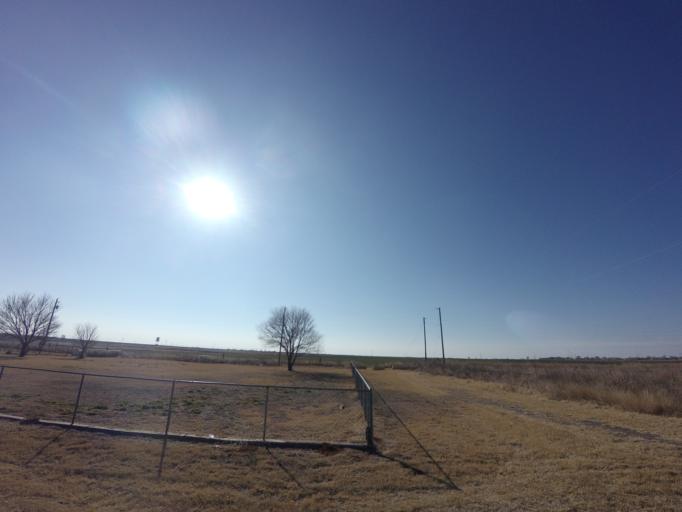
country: US
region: New Mexico
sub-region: Curry County
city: Clovis
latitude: 34.3834
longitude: -103.1847
